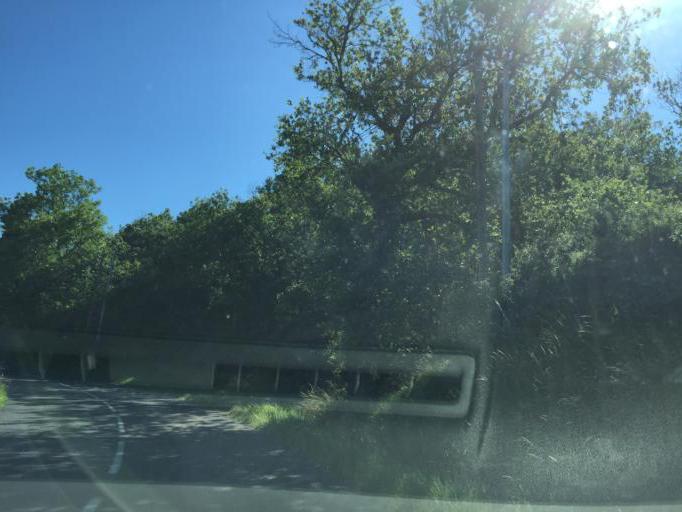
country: FR
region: Rhone-Alpes
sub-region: Departement du Rhone
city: Saint-Andeol-le-Chateau
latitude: 45.5660
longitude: 4.6991
